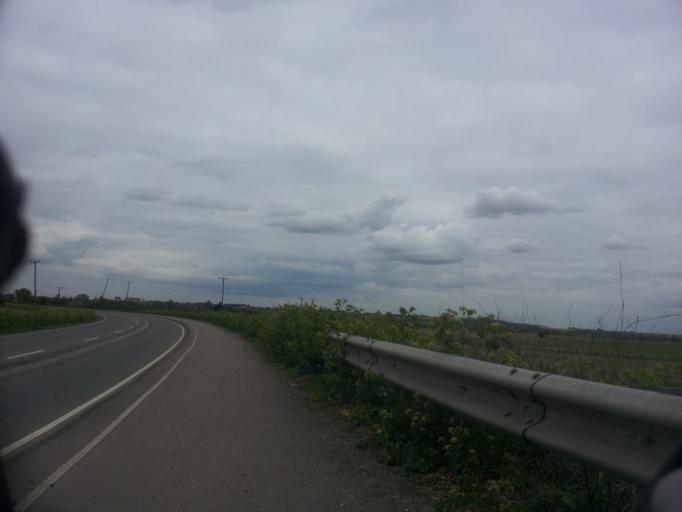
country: GB
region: England
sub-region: Kent
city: Queenborough
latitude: 51.4023
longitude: 0.7697
